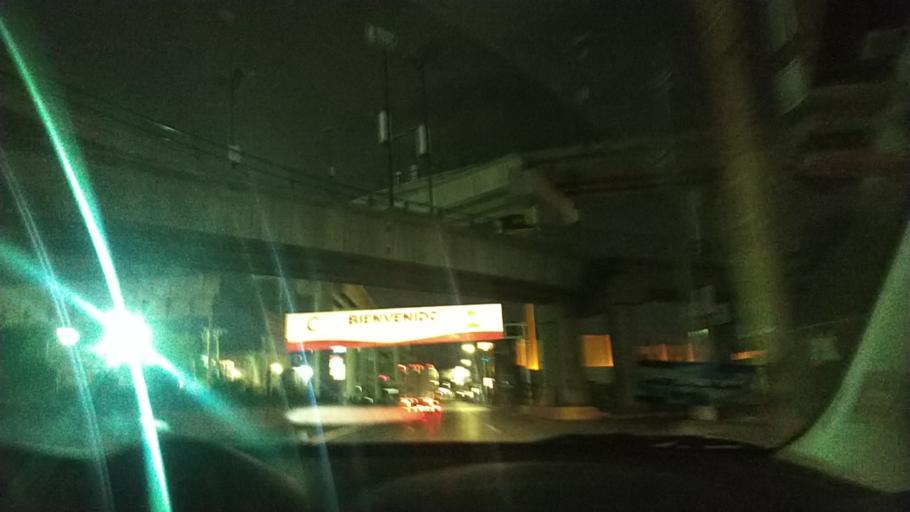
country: MX
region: Mexico
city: Ecatepec
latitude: 19.6264
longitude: -99.0793
